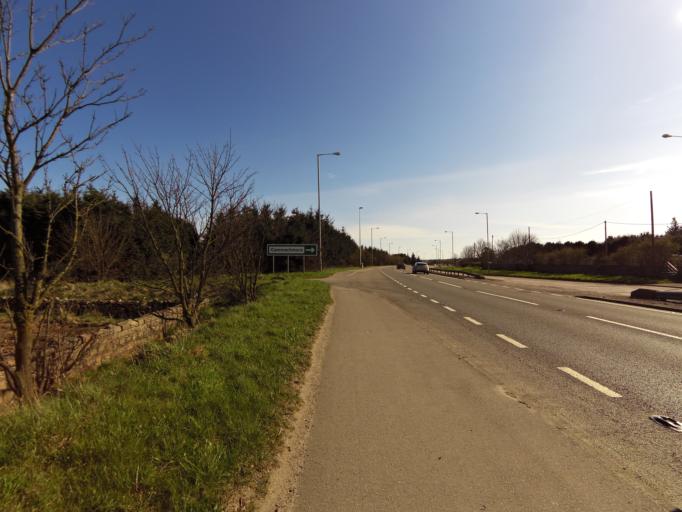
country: GB
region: Scotland
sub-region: Aberdeenshire
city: Newtonhill
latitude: 57.0497
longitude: -2.1498
